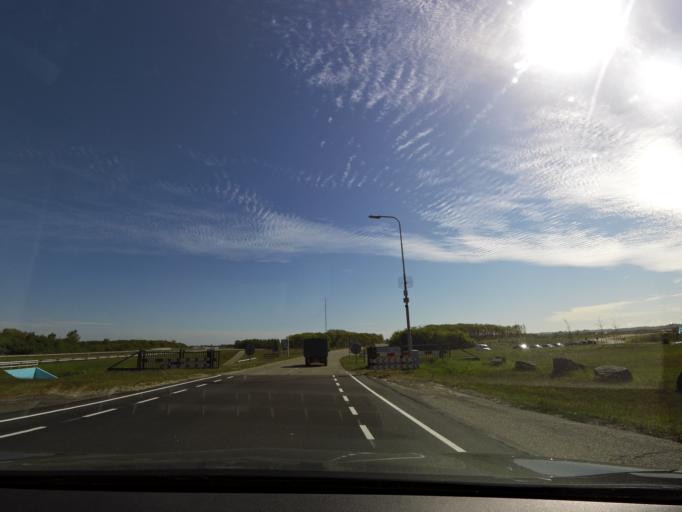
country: NL
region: Zeeland
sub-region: Schouwen-Duiveland
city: Scharendijke
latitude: 51.7394
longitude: 3.8243
